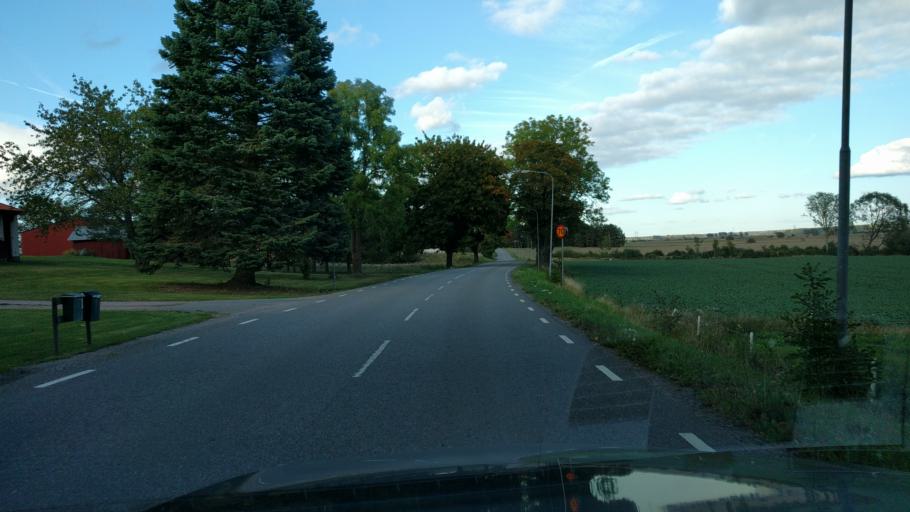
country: SE
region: Uppsala
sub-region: Osthammars Kommun
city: Bjorklinge
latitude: 60.1454
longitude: 17.5774
